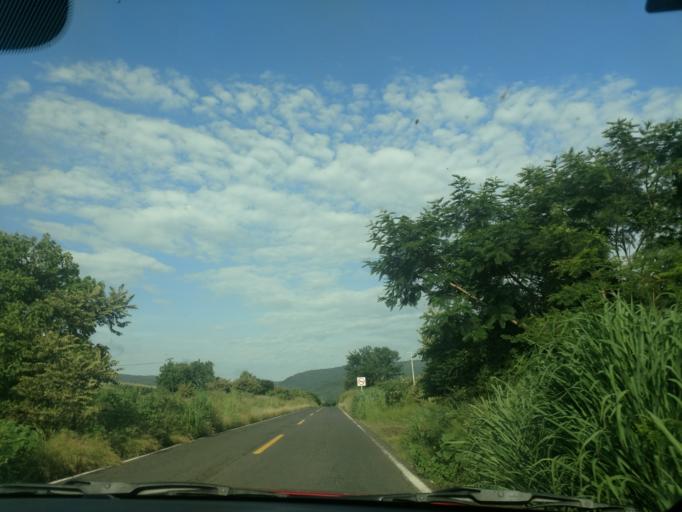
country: MX
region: Jalisco
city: Ameca
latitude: 20.5200
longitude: -104.1146
